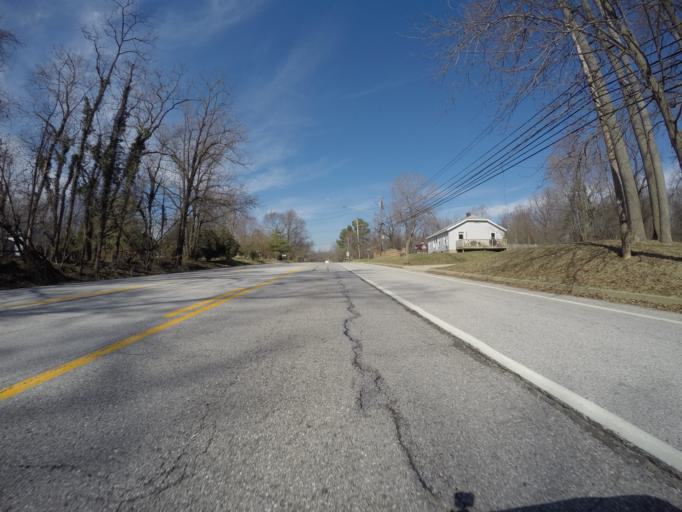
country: US
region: Maryland
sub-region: Anne Arundel County
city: Crownsville
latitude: 39.0336
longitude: -76.6032
